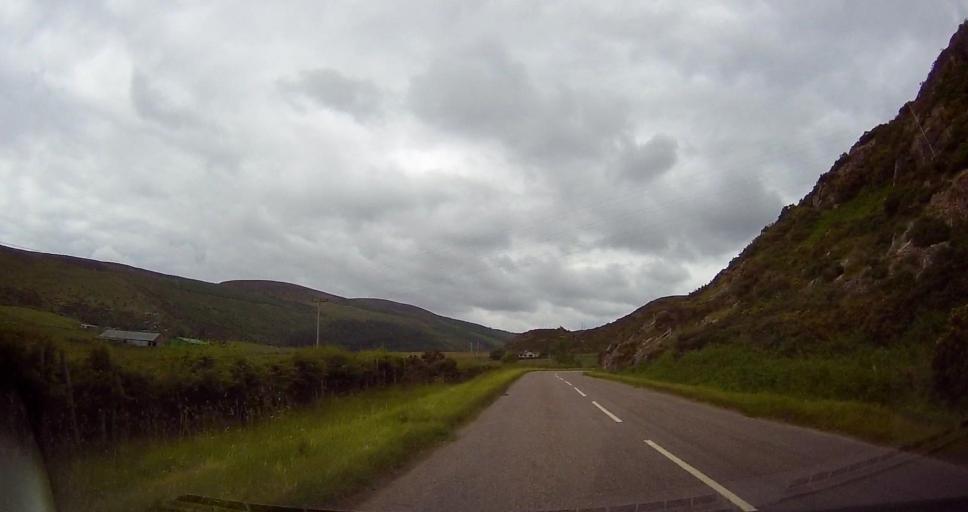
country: GB
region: Scotland
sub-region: Highland
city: Dornoch
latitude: 57.9829
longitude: -4.1279
